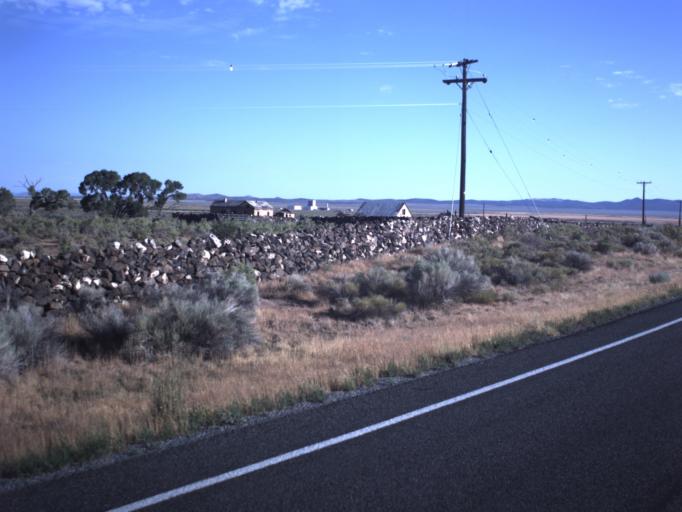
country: US
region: Utah
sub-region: Iron County
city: Enoch
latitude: 37.8561
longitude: -113.0318
